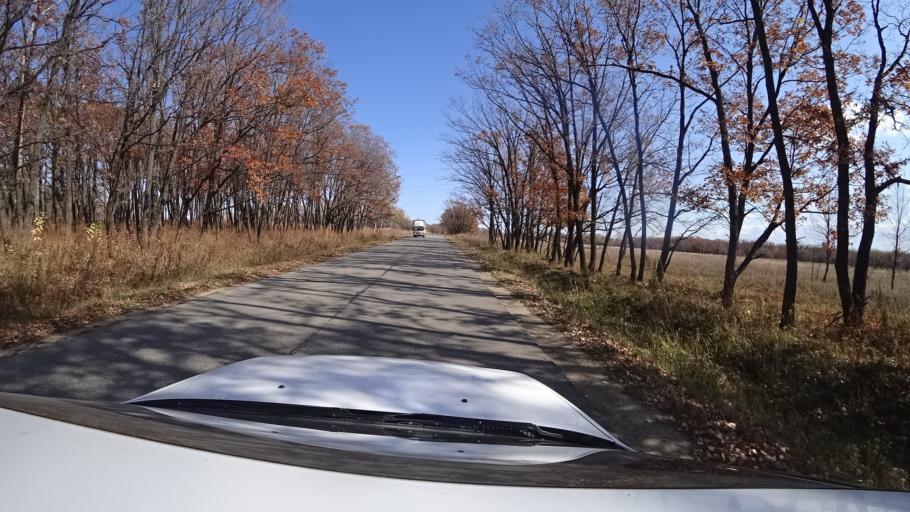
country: RU
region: Primorskiy
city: Lazo
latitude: 45.8683
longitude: 133.6632
